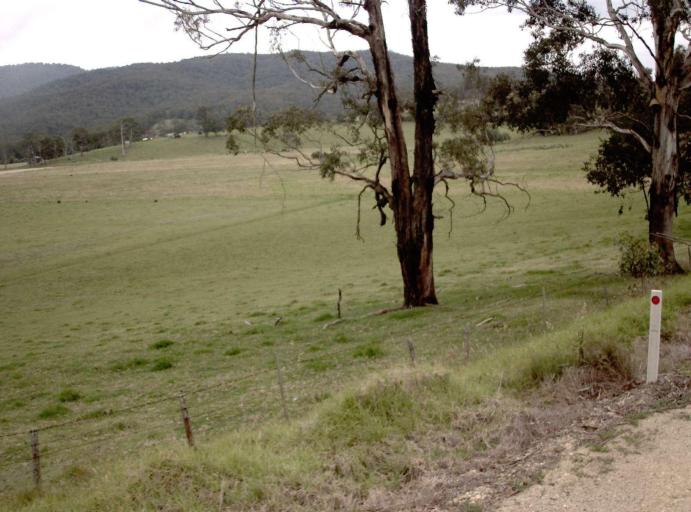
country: AU
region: New South Wales
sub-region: Bombala
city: Bombala
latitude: -37.4823
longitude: 149.1803
